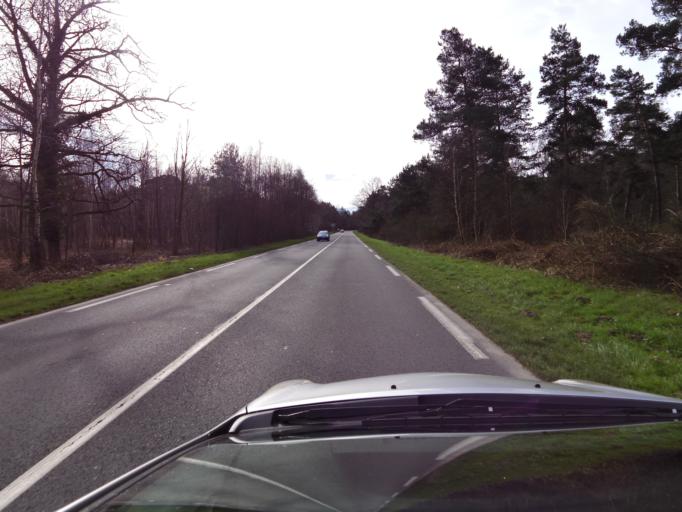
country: FR
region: Picardie
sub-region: Departement de l'Oise
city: Ver-sur-Launette
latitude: 49.1405
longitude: 2.6851
